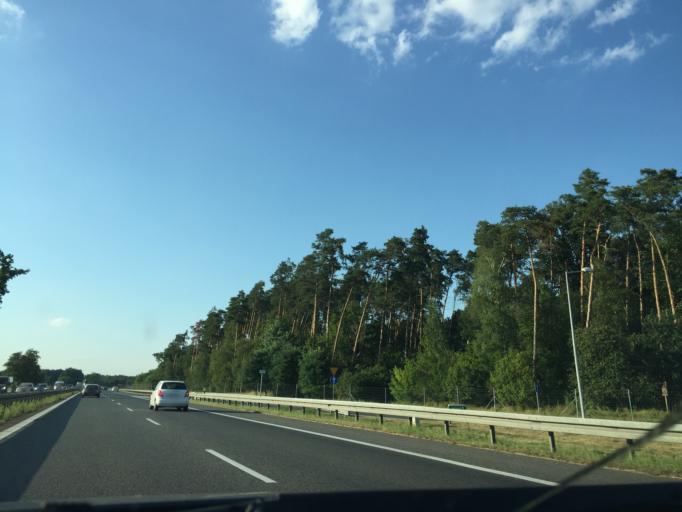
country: PL
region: Masovian Voivodeship
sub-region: Powiat bialobrzeski
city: Sucha
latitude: 51.6232
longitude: 20.9726
